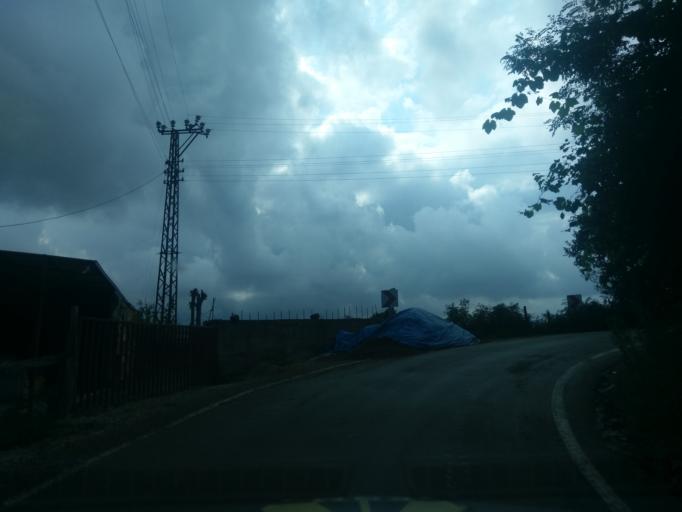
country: TR
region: Ordu
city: Camas
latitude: 40.8882
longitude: 37.6191
